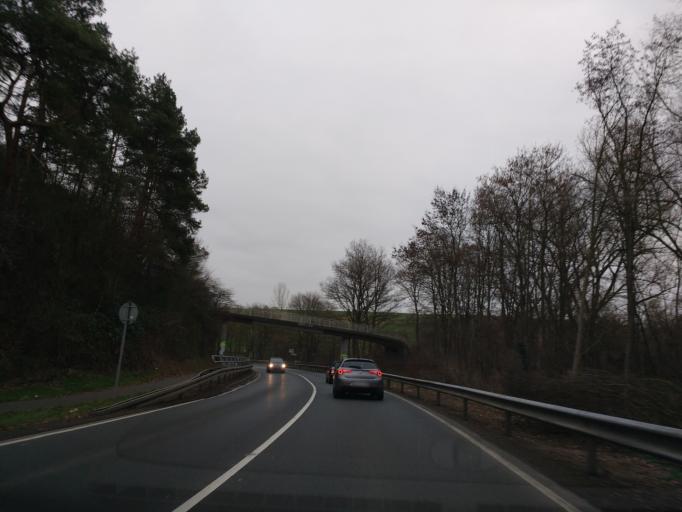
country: DE
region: Hesse
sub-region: Regierungsbezirk Kassel
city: Baunatal
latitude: 51.2126
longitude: 9.4353
